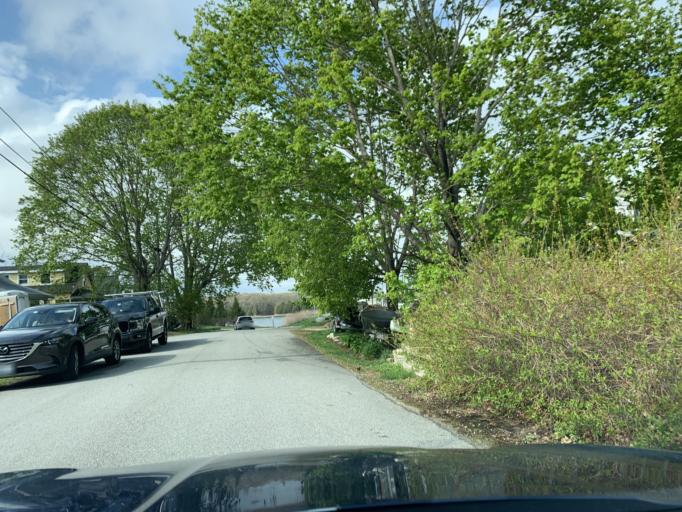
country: US
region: Rhode Island
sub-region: Washington County
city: North Kingstown
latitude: 41.5767
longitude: -71.4515
